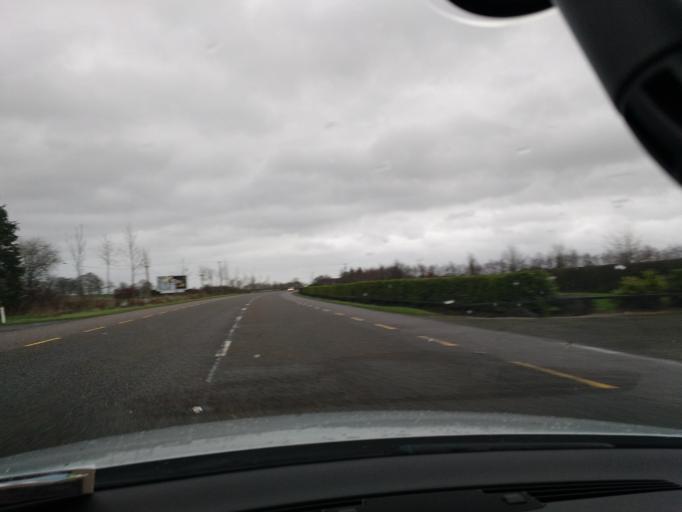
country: IE
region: Munster
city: Thurles
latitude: 52.6842
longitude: -7.6669
